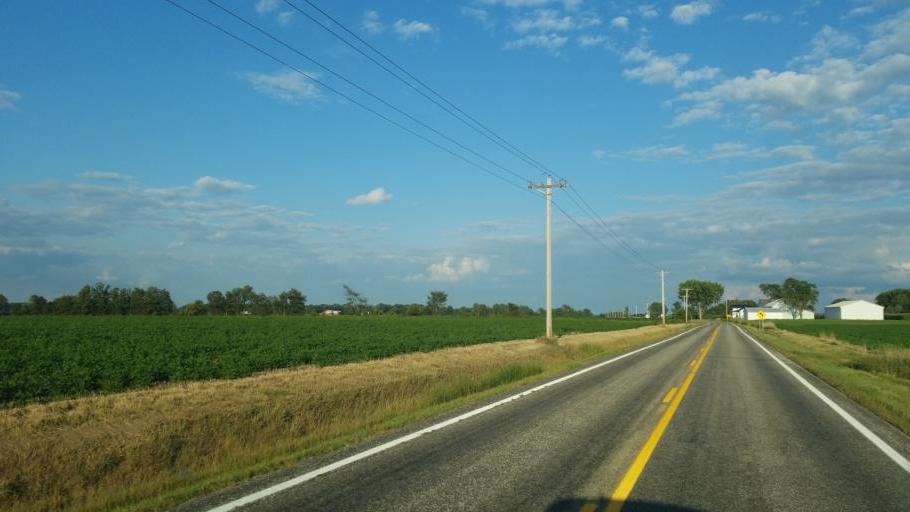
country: US
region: Ohio
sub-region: Huron County
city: Willard
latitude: 41.1064
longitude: -82.7673
